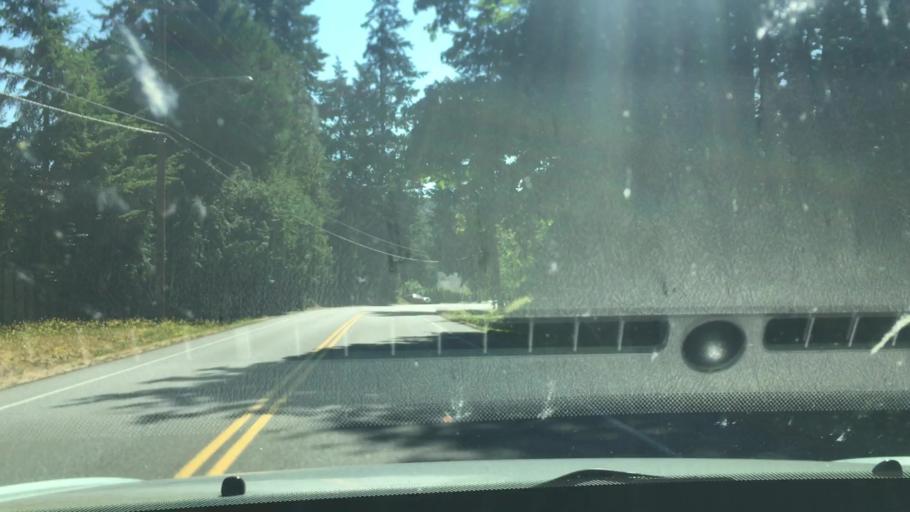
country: US
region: Washington
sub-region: King County
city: Newcastle
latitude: 47.5409
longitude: -122.1721
